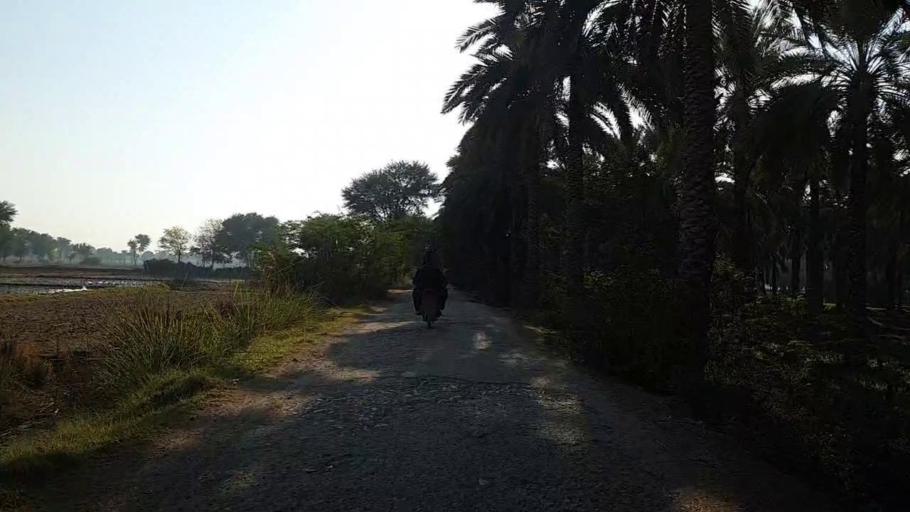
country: PK
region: Sindh
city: Ranipur
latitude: 27.2429
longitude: 68.5372
